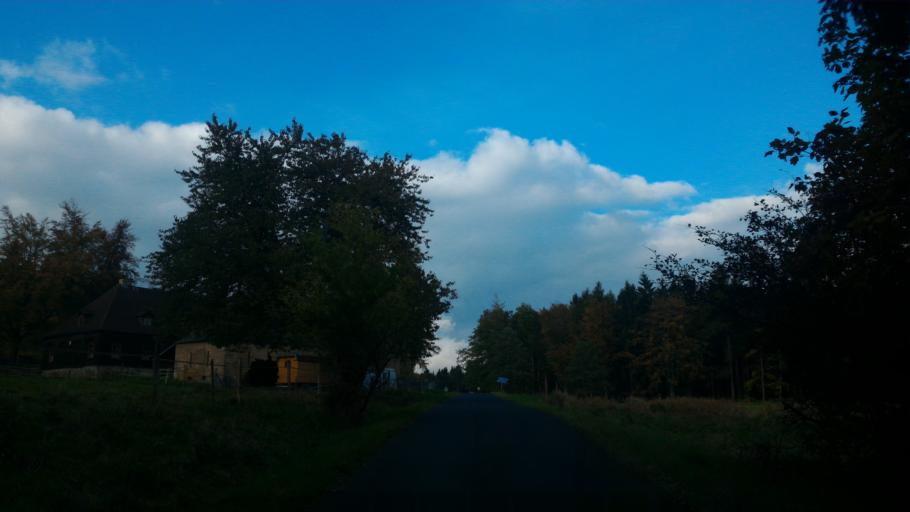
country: CZ
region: Ustecky
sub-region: Okres Decin
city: Chribska
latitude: 50.8307
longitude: 14.4909
